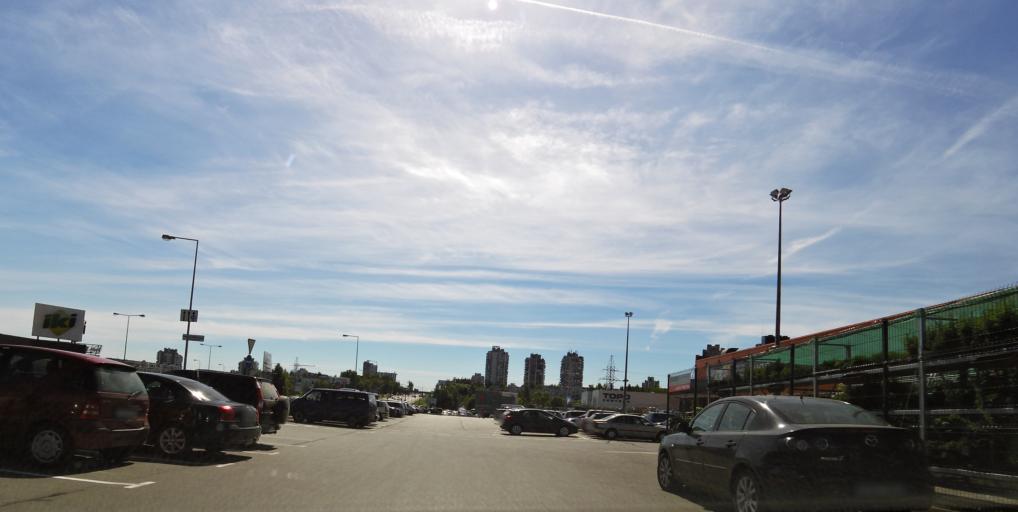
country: LT
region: Vilnius County
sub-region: Vilnius
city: Fabijoniskes
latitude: 54.7224
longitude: 25.2430
